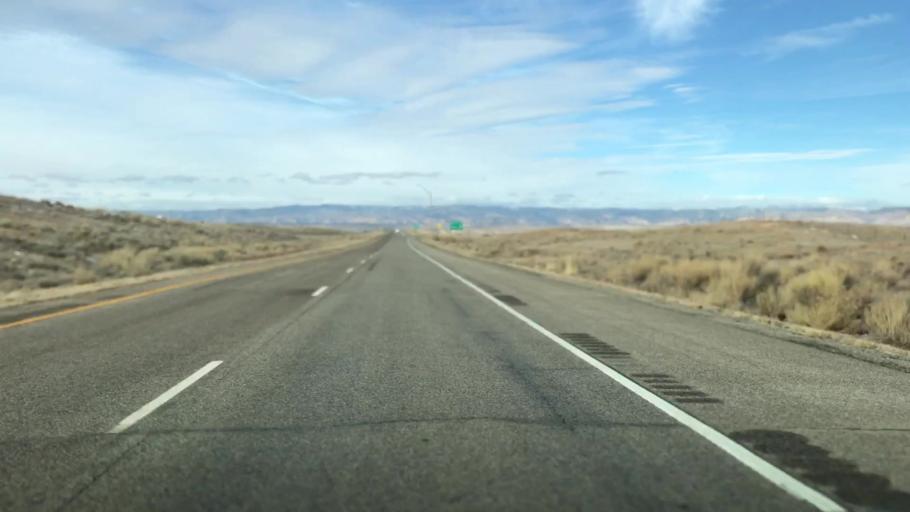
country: US
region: Colorado
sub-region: Mesa County
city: Loma
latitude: 39.2102
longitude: -108.8626
